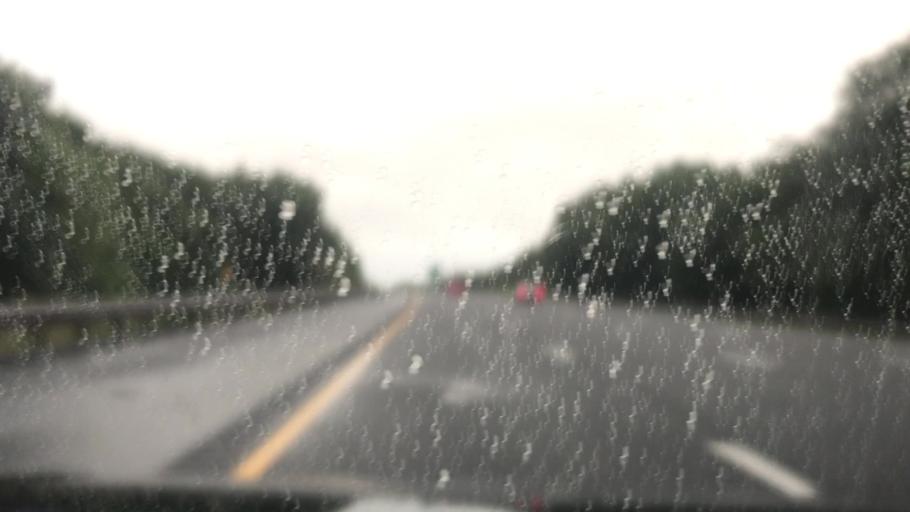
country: US
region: New Jersey
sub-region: Monmouth County
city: Ramtown
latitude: 40.1509
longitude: -74.1055
